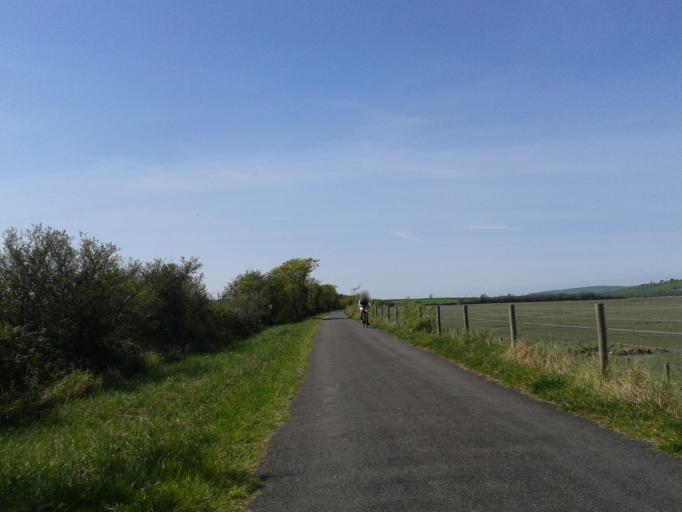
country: GB
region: England
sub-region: Devon
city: Fremington
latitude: 51.0799
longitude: -4.0945
